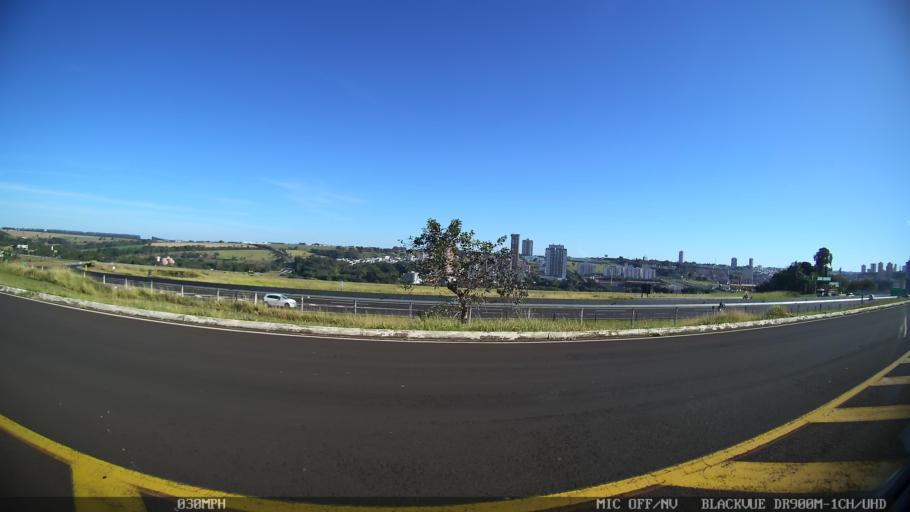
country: BR
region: Sao Paulo
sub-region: Franca
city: Franca
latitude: -20.5597
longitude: -47.4094
